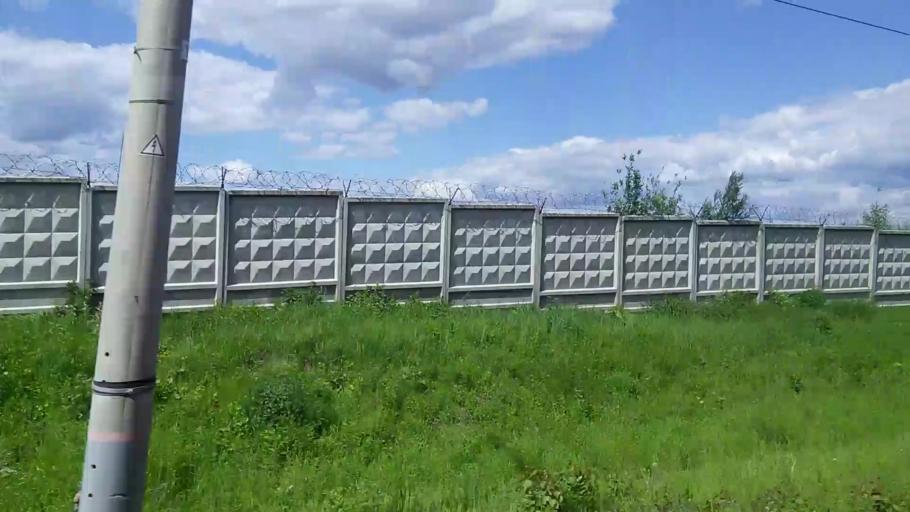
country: RU
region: Moskovskaya
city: Sheremet'yevskiy
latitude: 55.9734
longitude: 37.4501
